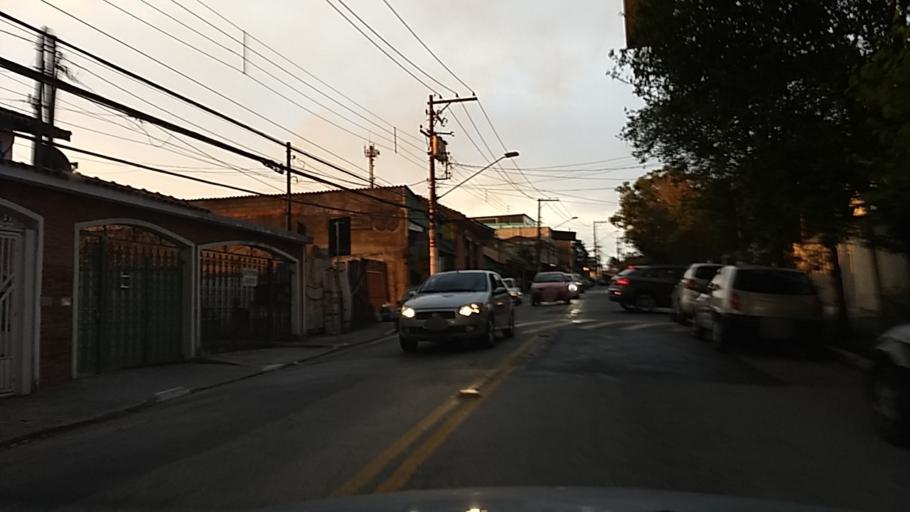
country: BR
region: Sao Paulo
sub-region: Osasco
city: Osasco
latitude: -23.4807
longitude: -46.7410
